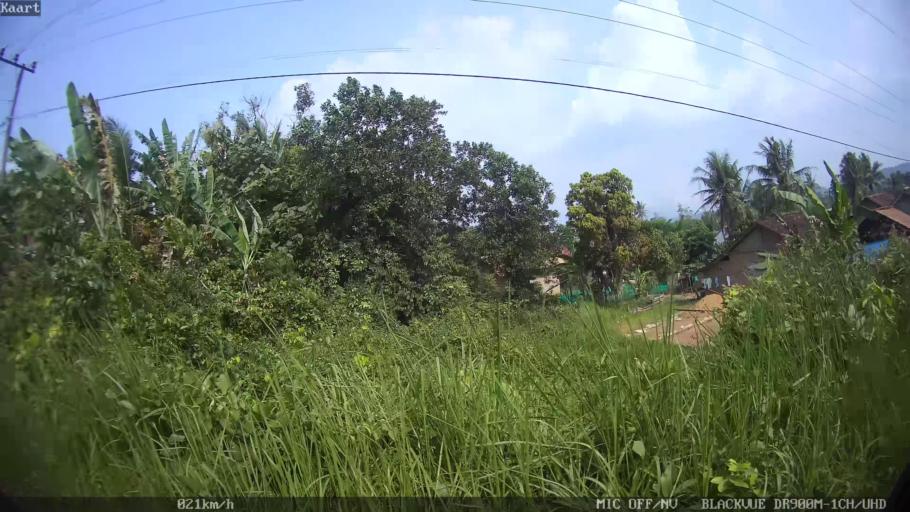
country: ID
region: Lampung
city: Pringsewu
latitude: -5.4050
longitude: 104.9924
